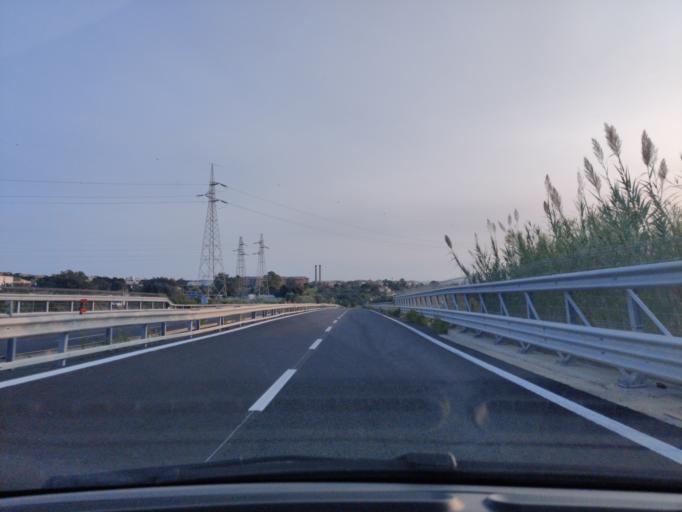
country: IT
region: Latium
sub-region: Citta metropolitana di Roma Capitale
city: Civitavecchia
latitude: 42.1120
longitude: 11.7924
